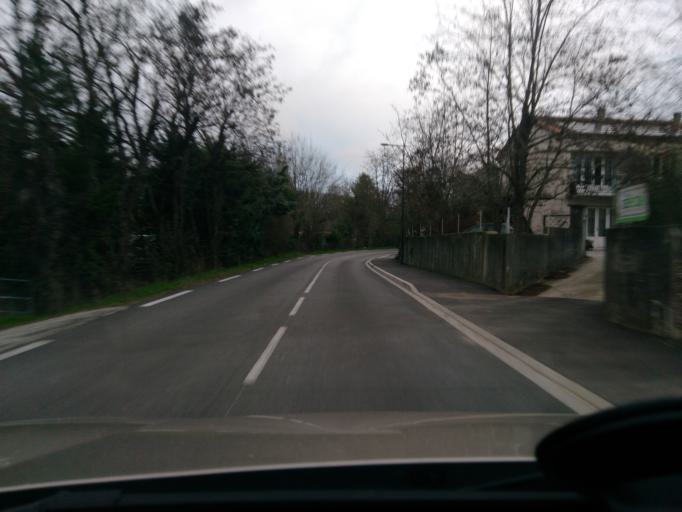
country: FR
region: Rhone-Alpes
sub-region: Departement de la Drome
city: Montelimar
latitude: 44.5576
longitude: 4.7650
